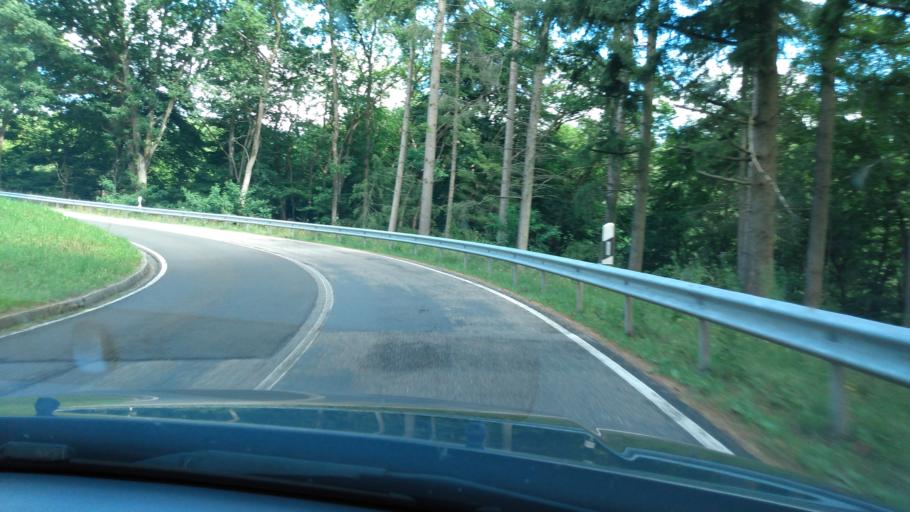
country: DE
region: Rheinland-Pfalz
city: Hupperath
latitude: 49.9995
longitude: 6.8540
